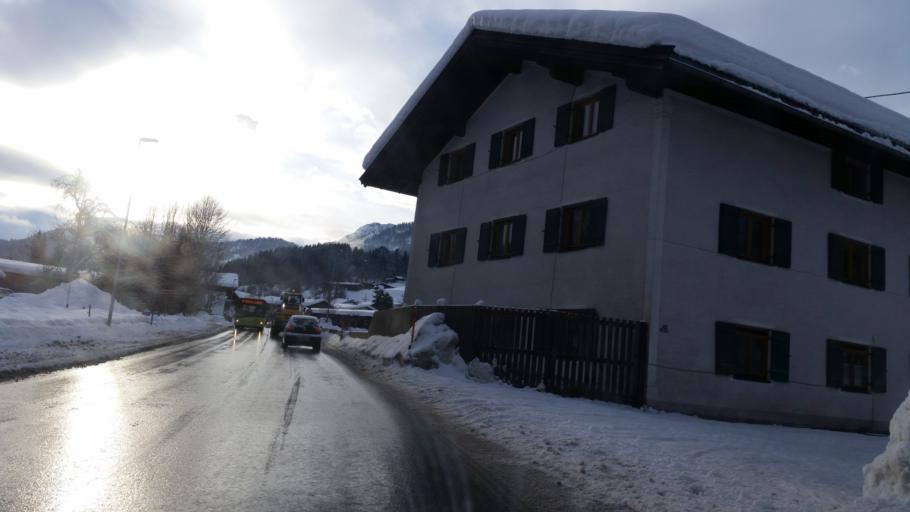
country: AT
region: Tyrol
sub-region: Politischer Bezirk Kitzbuhel
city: Fieberbrunn
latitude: 47.4833
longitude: 12.5348
